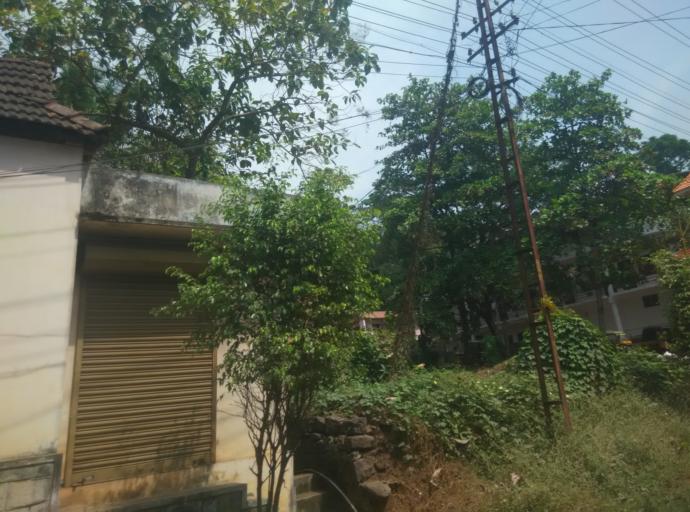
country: IN
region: Kerala
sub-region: Kottayam
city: Palackattumala
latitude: 9.6986
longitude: 76.6509
